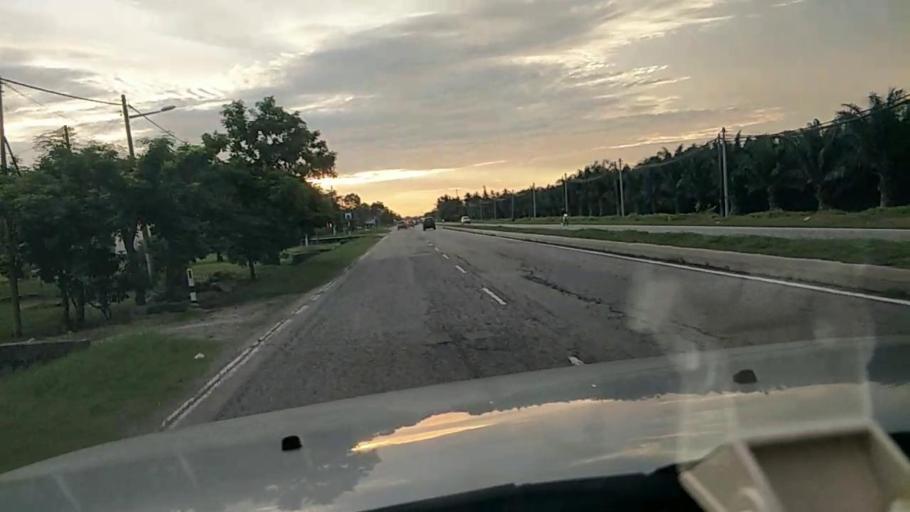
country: MY
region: Perak
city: Kampong Dungun
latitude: 3.1427
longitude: 101.3592
